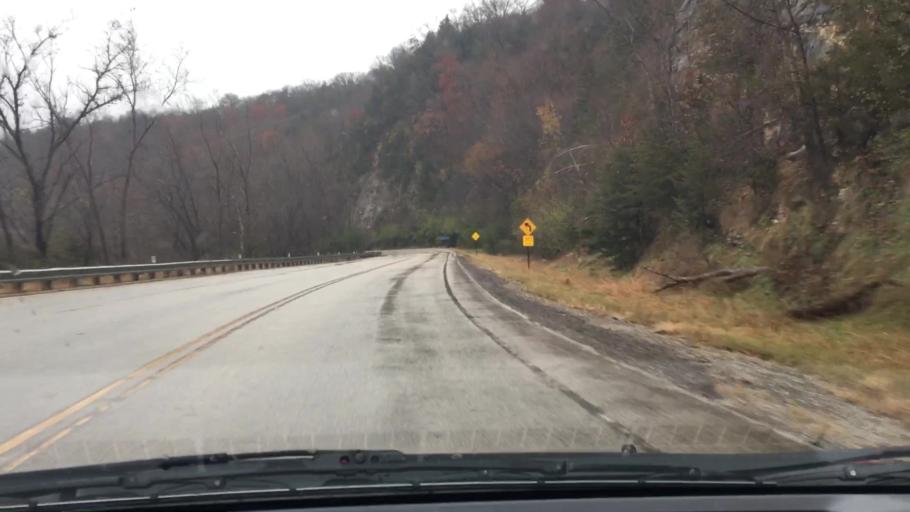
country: US
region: Minnesota
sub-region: Fillmore County
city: Preston
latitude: 43.7238
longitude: -91.9801
